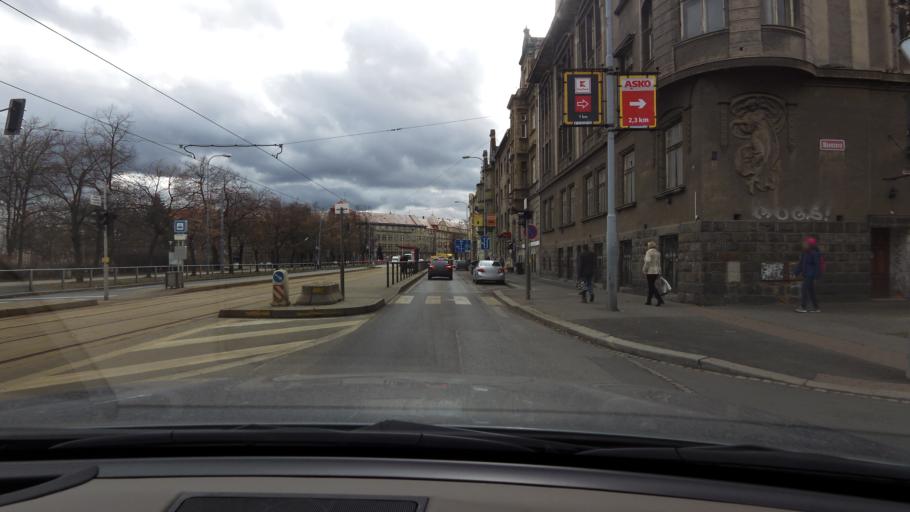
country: CZ
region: Plzensky
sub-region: Okres Plzen-Mesto
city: Pilsen
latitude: 49.7315
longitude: 13.3700
